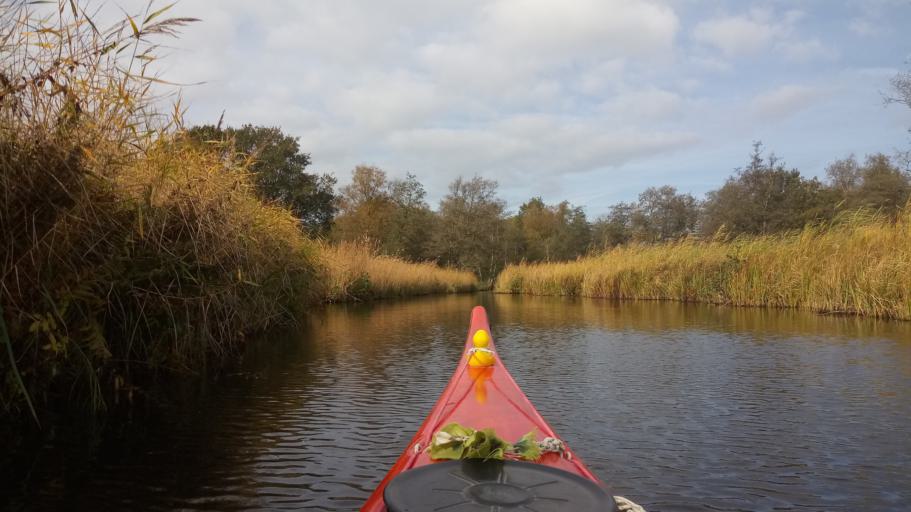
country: NL
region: Overijssel
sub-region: Gemeente Steenwijkerland
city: Sint Jansklooster
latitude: 52.6687
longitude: 6.0321
